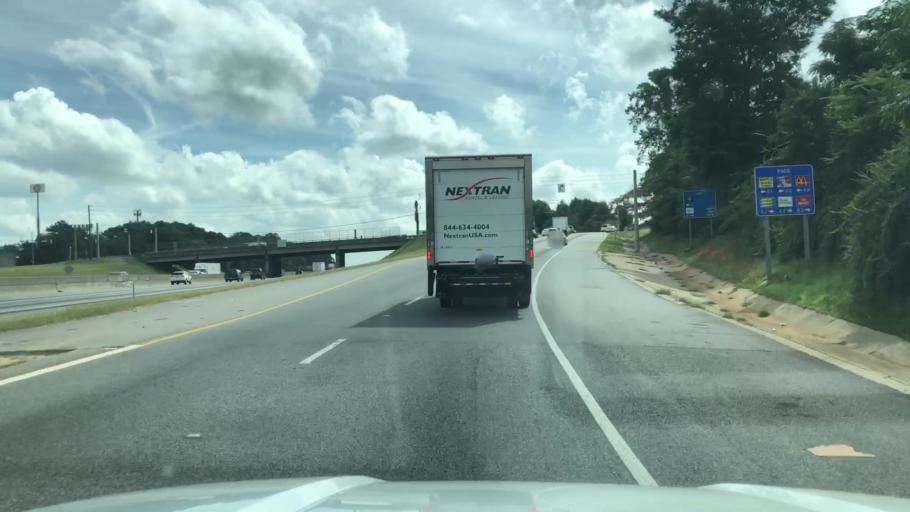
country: US
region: Georgia
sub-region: DeKalb County
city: Redan
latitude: 33.7032
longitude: -84.1727
